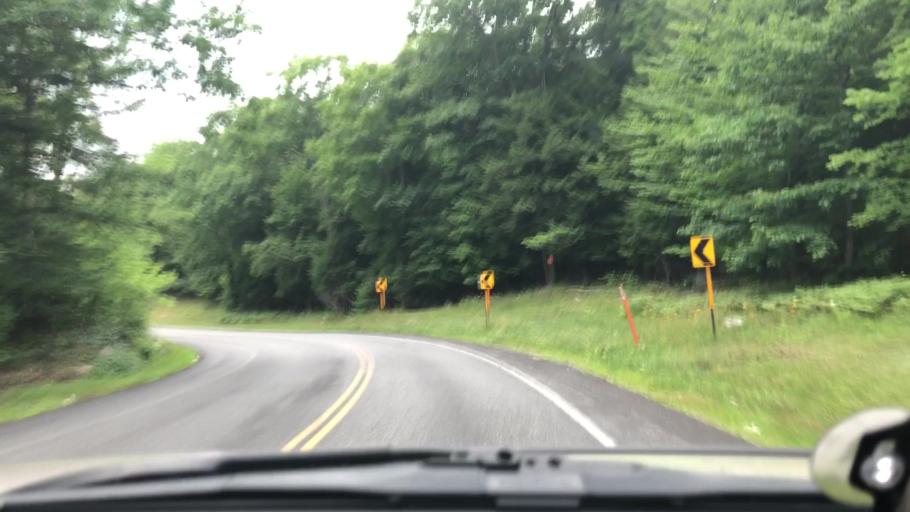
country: US
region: New York
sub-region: Saratoga County
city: Corinth
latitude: 43.1970
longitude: -73.7592
